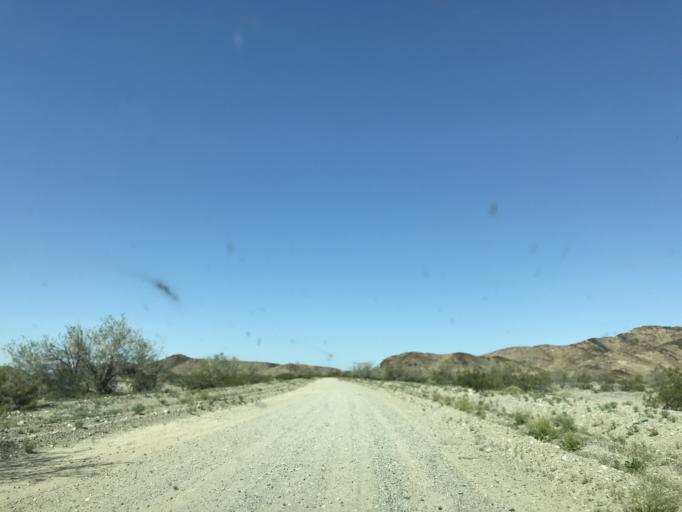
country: US
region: California
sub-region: Riverside County
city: Mesa Verde
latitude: 33.4902
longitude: -114.7809
